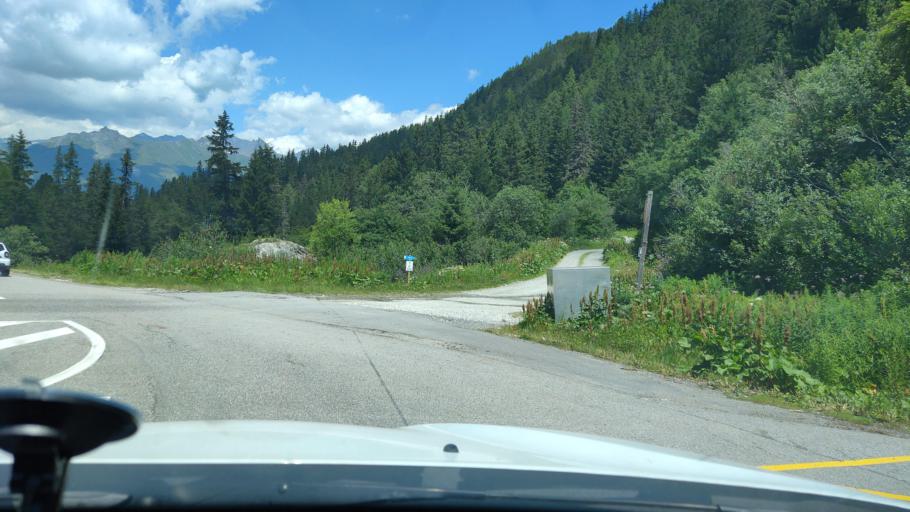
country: FR
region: Rhone-Alpes
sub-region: Departement de la Savoie
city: Seez
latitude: 45.5832
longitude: 6.8351
